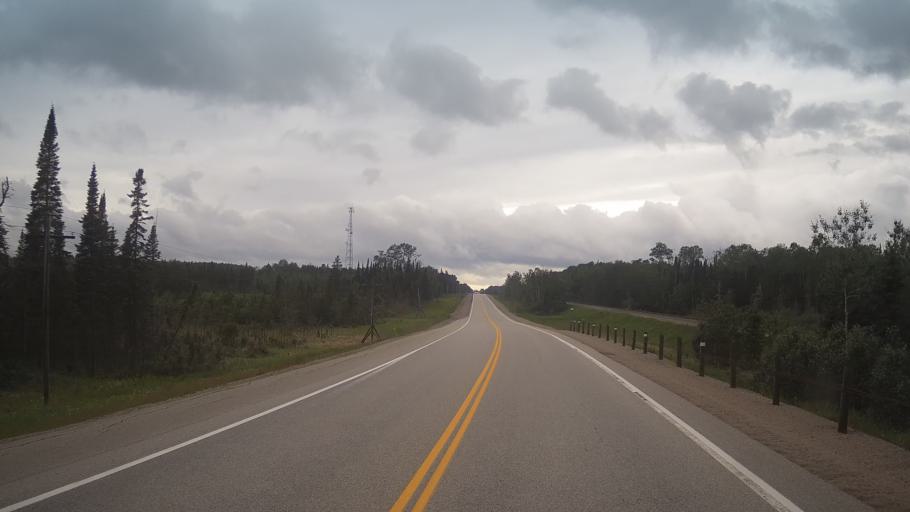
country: CA
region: Ontario
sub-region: Thunder Bay District
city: Thunder Bay
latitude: 48.9358
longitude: -90.1319
